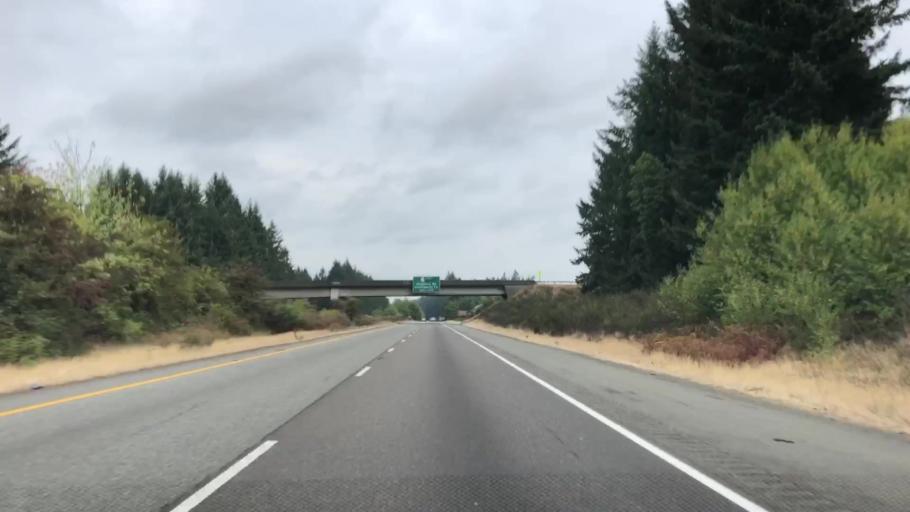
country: US
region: Washington
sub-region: Kitsap County
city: Bethel
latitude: 47.4835
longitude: -122.6294
